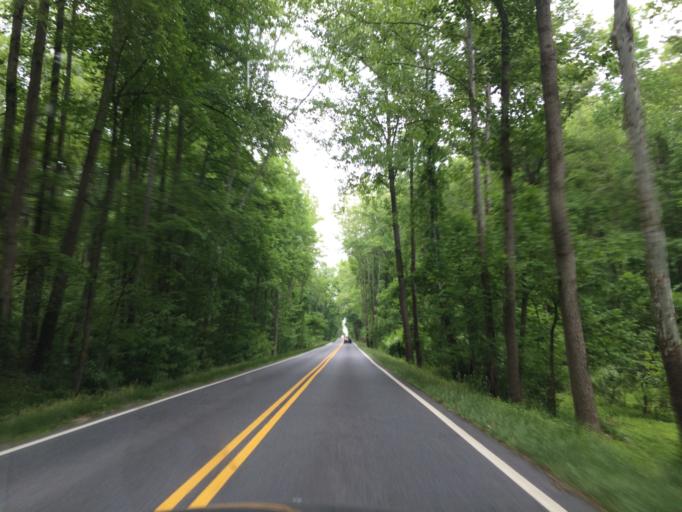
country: US
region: Maryland
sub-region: Carroll County
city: Eldersburg
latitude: 39.3561
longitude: -76.8950
